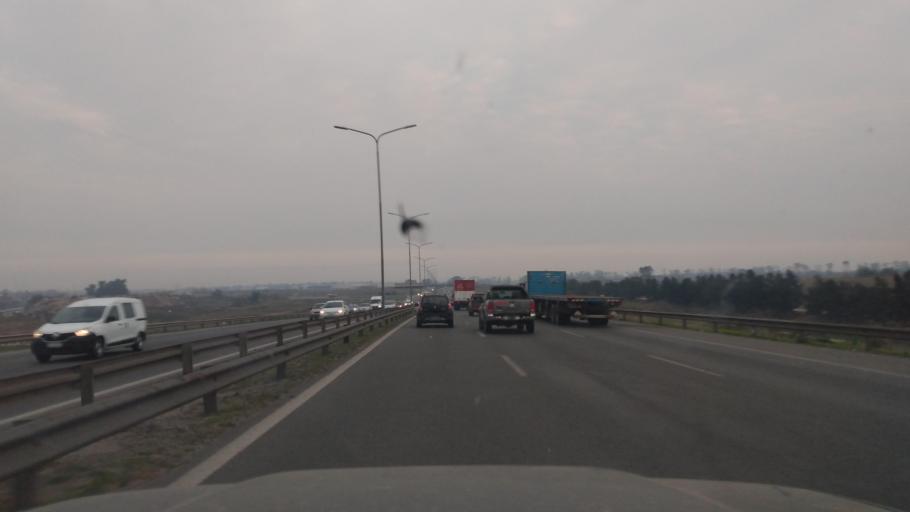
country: AR
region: Buenos Aires
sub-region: Partido de Tigre
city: Tigre
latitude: -34.5108
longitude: -58.5904
